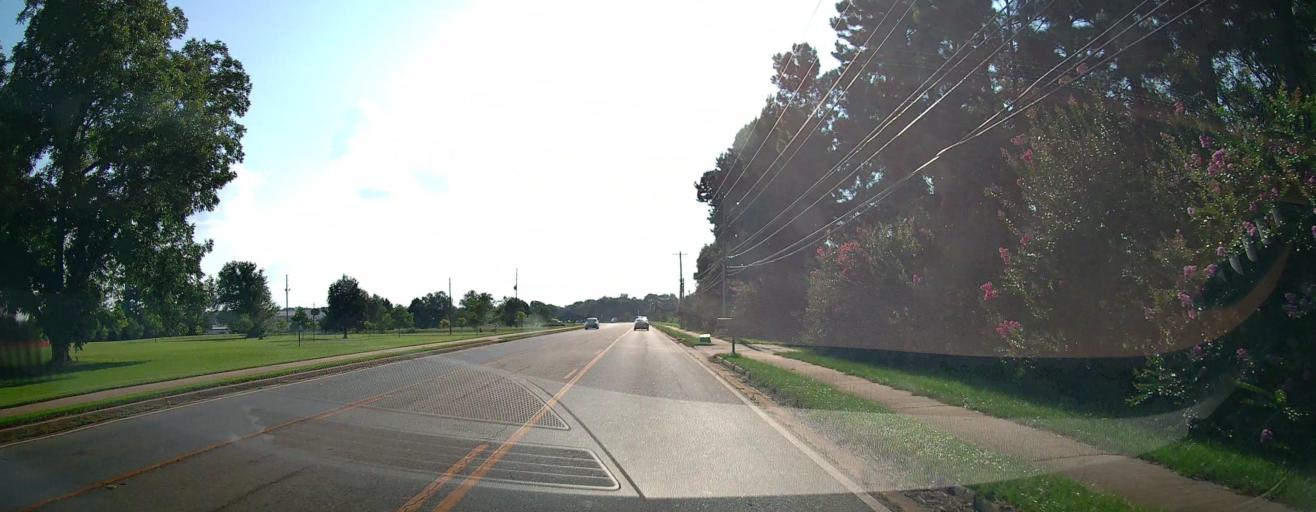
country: US
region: Georgia
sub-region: Houston County
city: Perry
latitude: 32.5062
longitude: -83.6567
